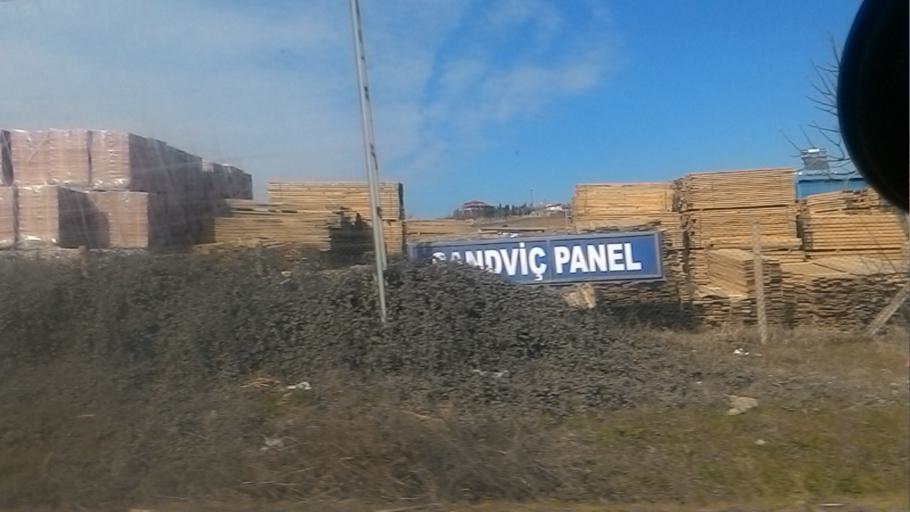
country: TR
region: Istanbul
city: Canta
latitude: 41.0772
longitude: 28.0775
